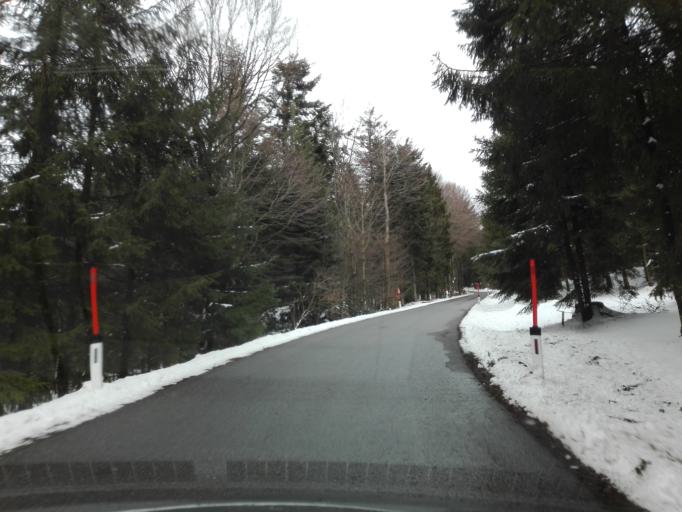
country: AT
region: Upper Austria
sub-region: Politischer Bezirk Rohrbach
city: Pfarrkirchen im Muehlkreis
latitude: 48.5530
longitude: 13.8303
